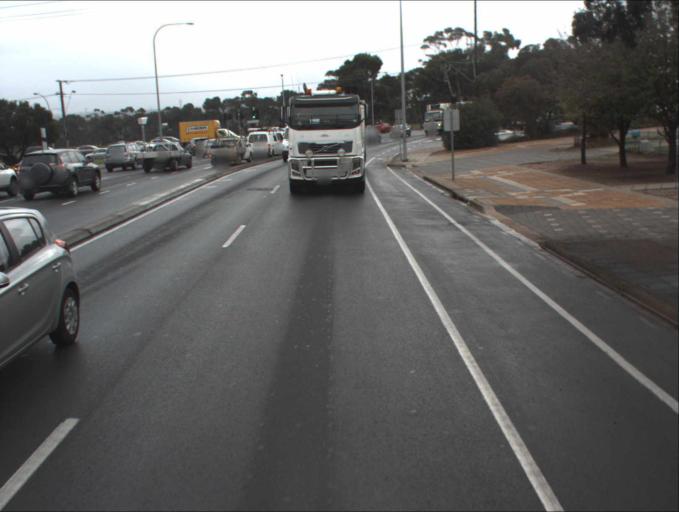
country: AU
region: South Australia
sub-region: Port Adelaide Enfield
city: Enfield
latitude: -34.8482
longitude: 138.6174
